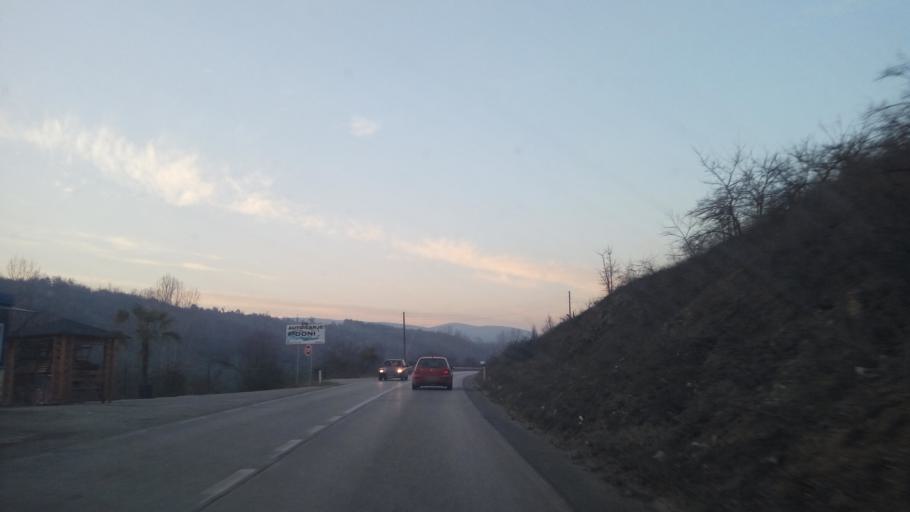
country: XK
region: Gjilan
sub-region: Komuna e Gjilanit
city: Gjilan
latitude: 42.4921
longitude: 21.3900
